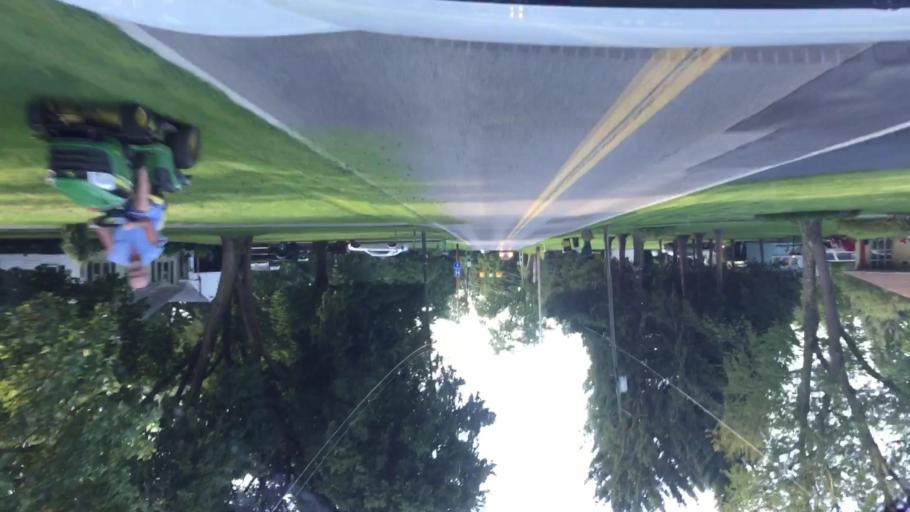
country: US
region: Ohio
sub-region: Clark County
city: Northridge
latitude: 39.9397
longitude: -83.7302
